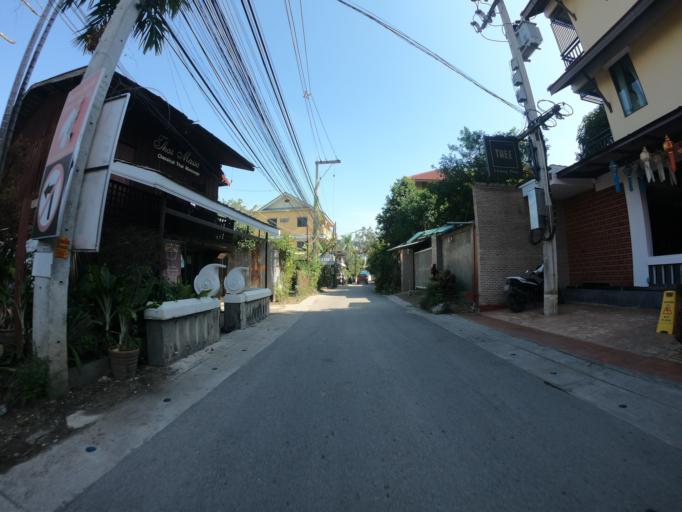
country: TH
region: Chiang Mai
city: Chiang Mai
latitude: 18.7798
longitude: 98.9949
